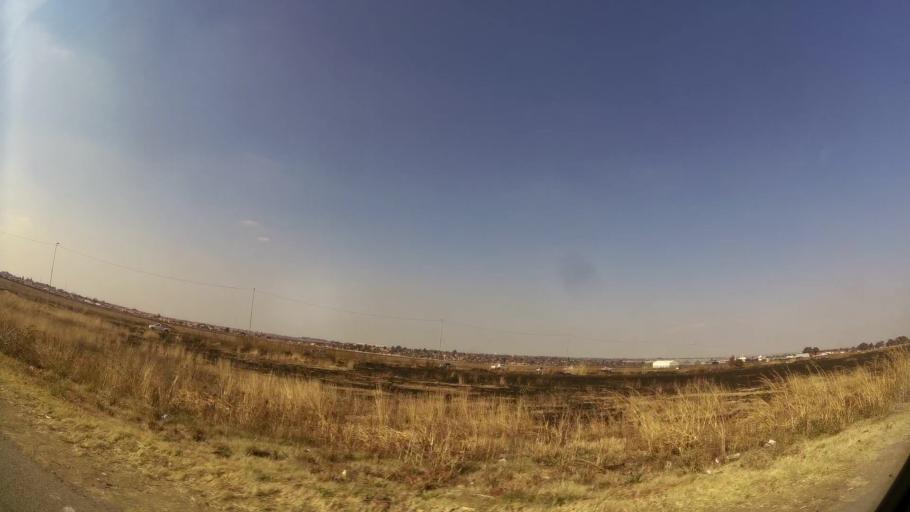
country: ZA
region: Gauteng
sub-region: Ekurhuleni Metropolitan Municipality
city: Boksburg
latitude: -26.2365
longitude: 28.2957
